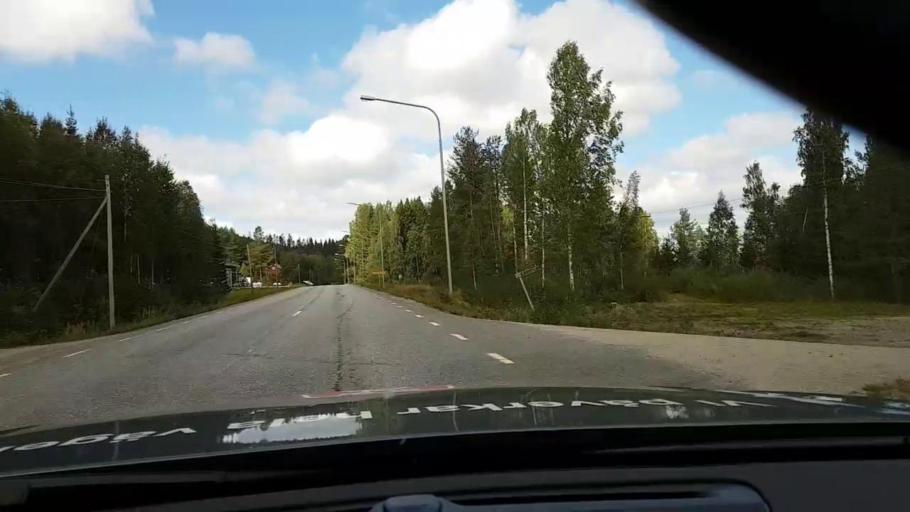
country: SE
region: Vaesternorrland
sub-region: OErnskoeldsviks Kommun
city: Bredbyn
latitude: 63.4888
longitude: 18.0836
